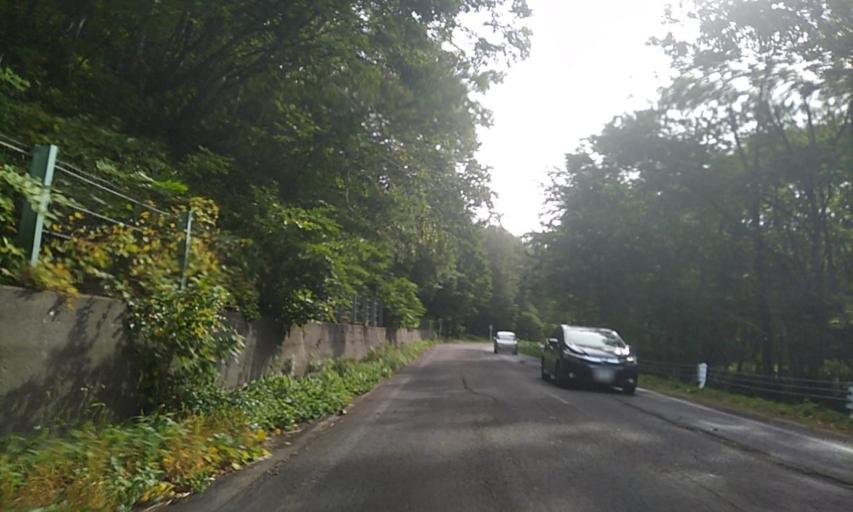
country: JP
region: Hokkaido
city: Abashiri
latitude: 43.6791
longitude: 144.5451
